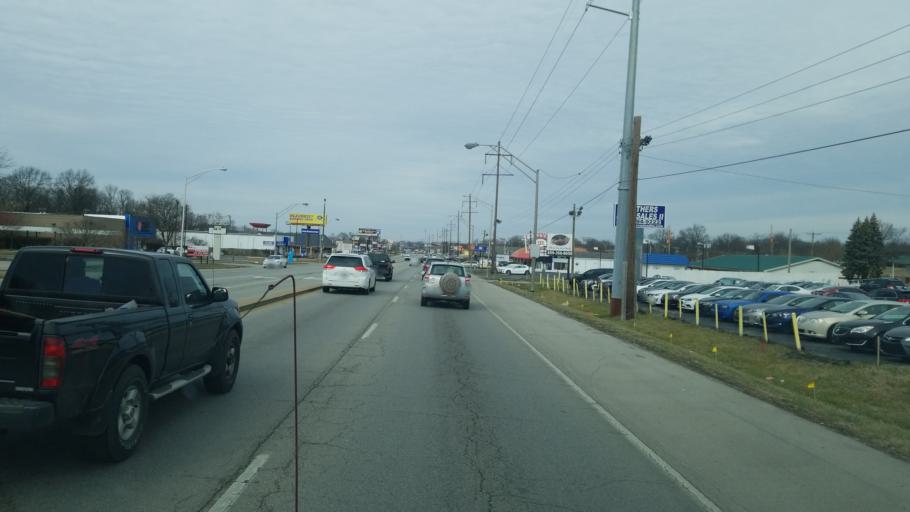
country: US
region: Kentucky
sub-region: Fayette County
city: Lexington-Fayette
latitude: 38.0608
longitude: -84.4655
